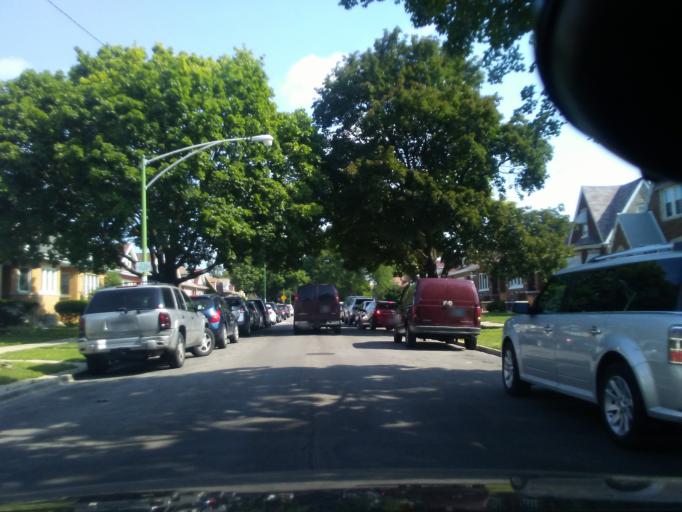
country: US
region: Illinois
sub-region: Cook County
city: Elmwood Park
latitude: 41.9334
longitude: -87.7687
